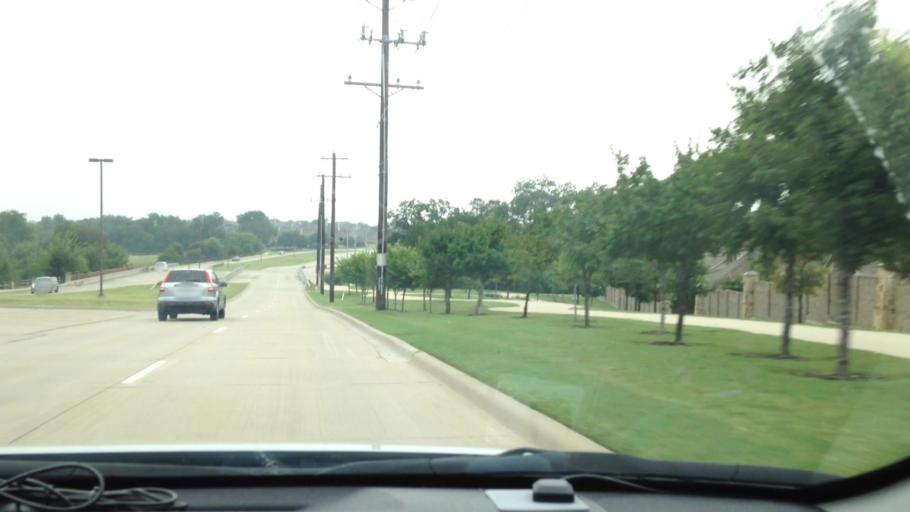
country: US
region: Texas
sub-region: Collin County
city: Allen
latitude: 33.1157
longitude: -96.7090
